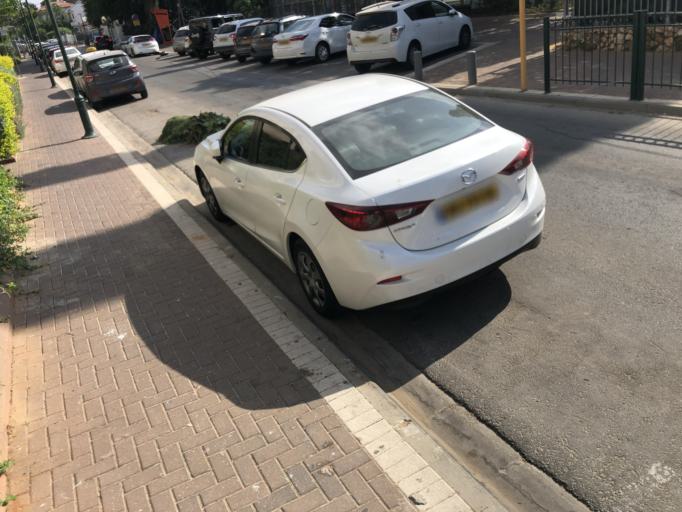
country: IL
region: Central District
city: Yehud
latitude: 32.0322
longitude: 34.8942
